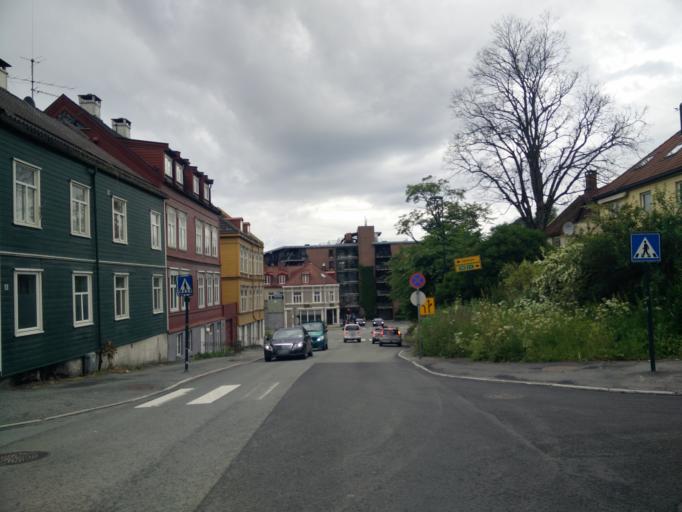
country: NO
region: Sor-Trondelag
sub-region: Trondheim
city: Trondheim
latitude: 63.4327
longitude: 10.4120
